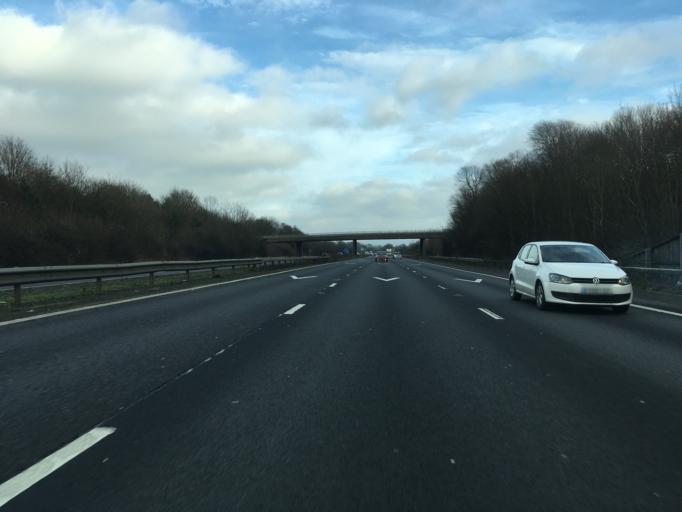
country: GB
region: England
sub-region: Gloucestershire
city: Barnwood
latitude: 51.8383
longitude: -2.1975
